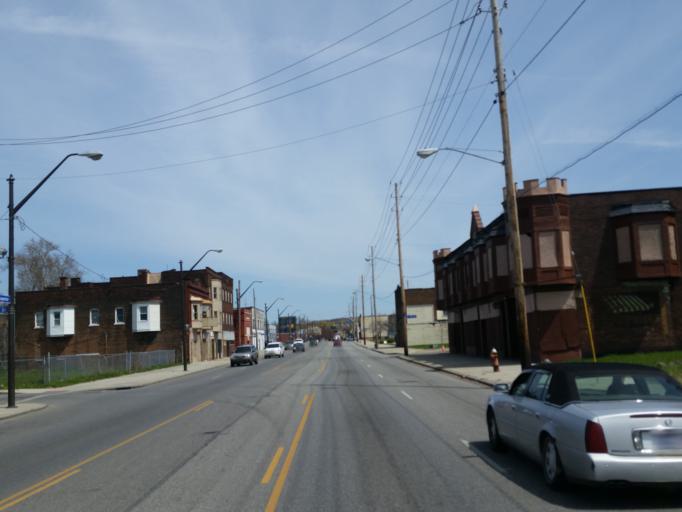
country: US
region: Ohio
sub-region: Cuyahoga County
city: Bratenahl
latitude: 41.5225
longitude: -81.6079
